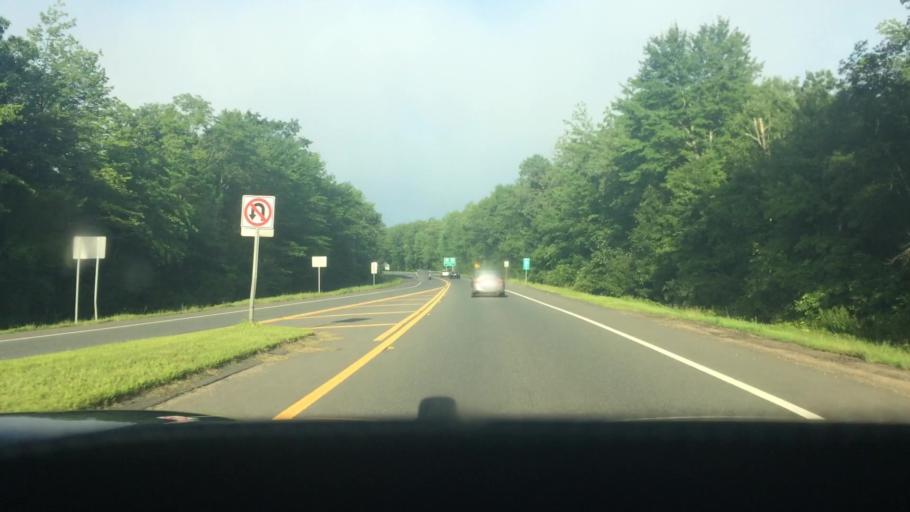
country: US
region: Massachusetts
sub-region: Franklin County
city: Turners Falls
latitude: 42.6149
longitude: -72.5629
